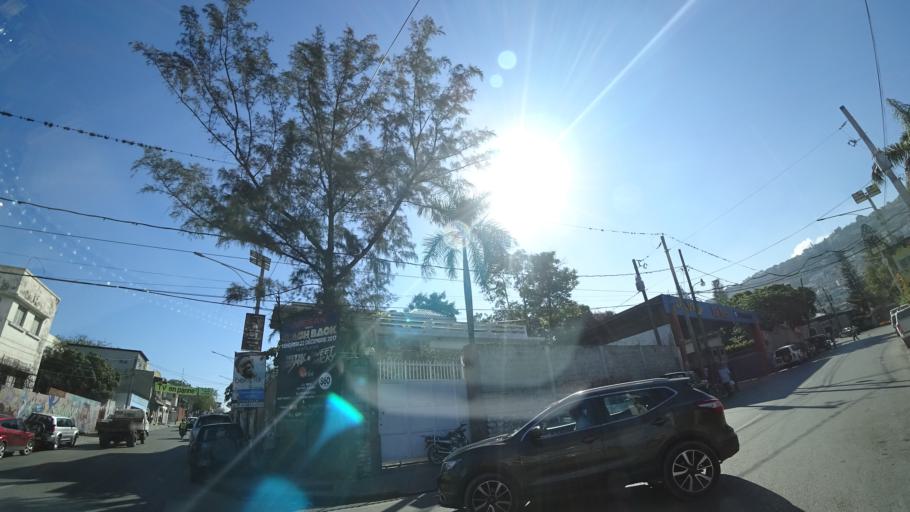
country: HT
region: Ouest
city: Petionville
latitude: 18.5153
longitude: -72.2918
